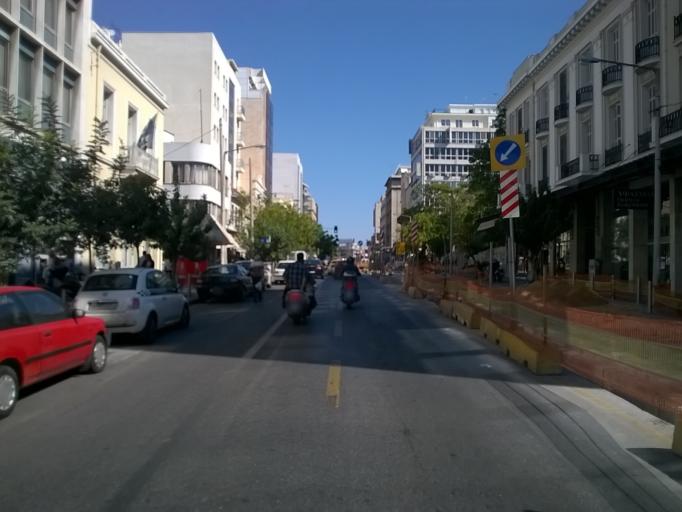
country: GR
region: Attica
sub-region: Nomos Attikis
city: Piraeus
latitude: 37.9453
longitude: 23.6454
